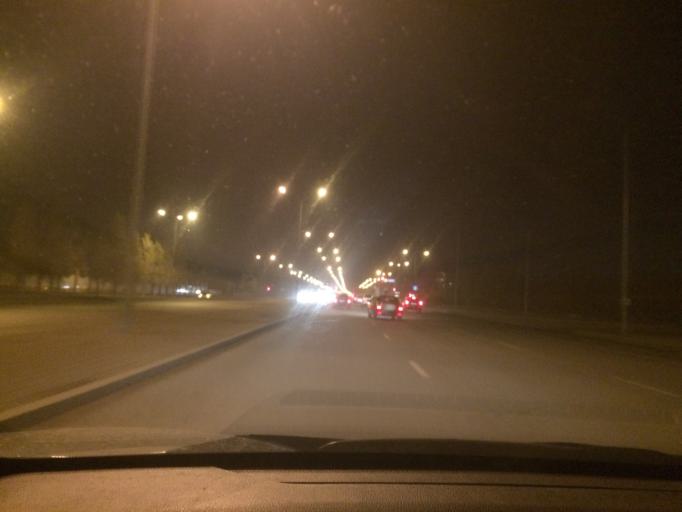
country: KZ
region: Astana Qalasy
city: Astana
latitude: 51.1846
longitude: 71.3611
